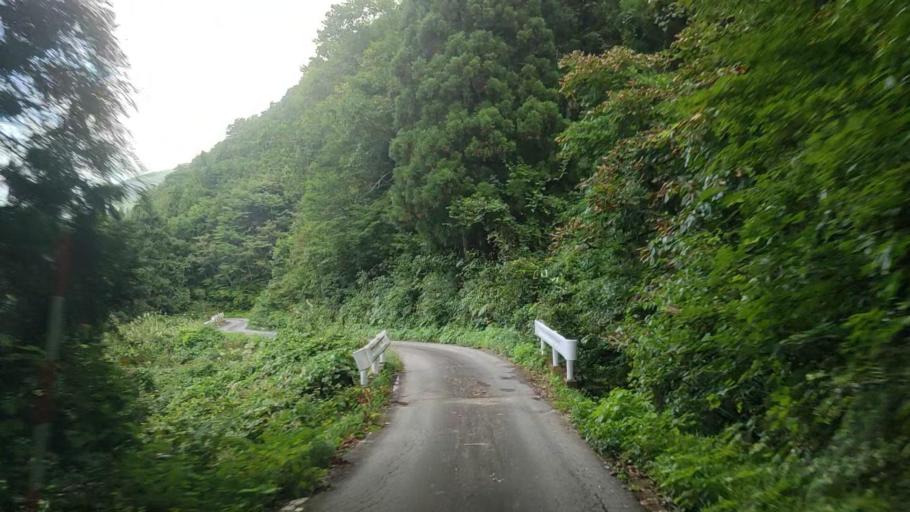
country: JP
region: Toyama
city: Yatsuomachi-higashikumisaka
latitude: 36.4123
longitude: 137.0796
